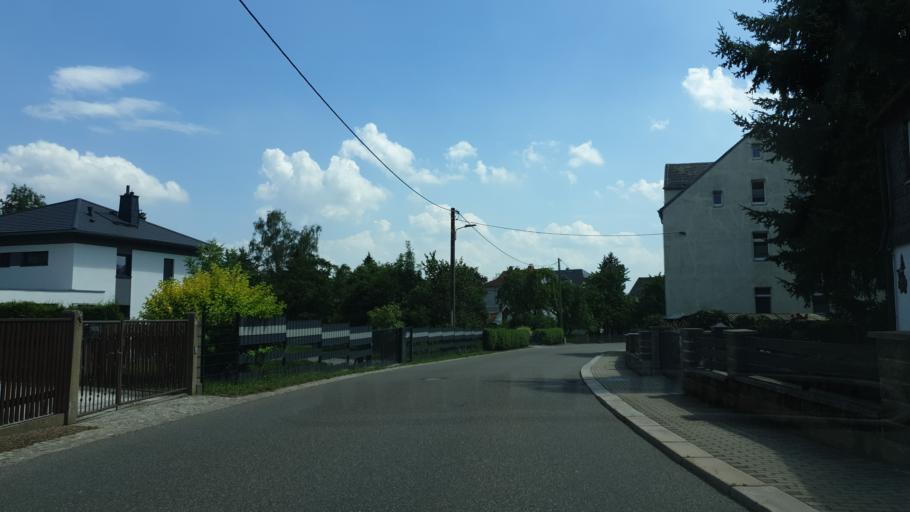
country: DE
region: Saxony
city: Hohenstein-Ernstthal
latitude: 50.8074
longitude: 12.7531
